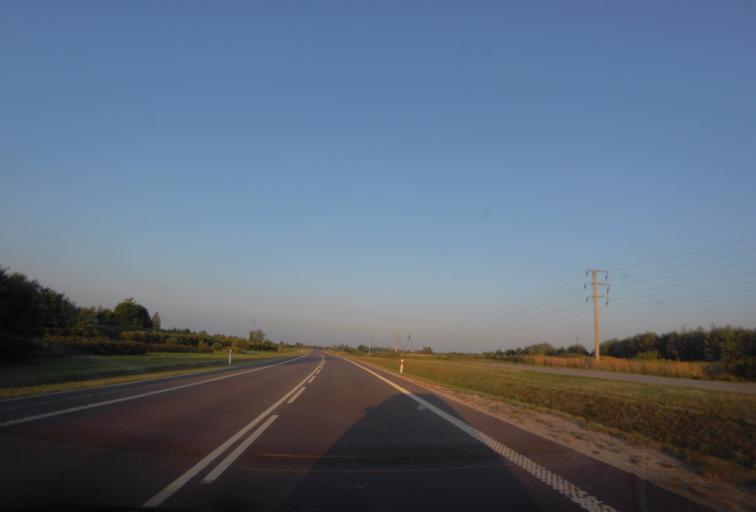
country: PL
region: Lublin Voivodeship
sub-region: Powiat bilgorajski
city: Frampol
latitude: 50.6768
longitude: 22.6615
